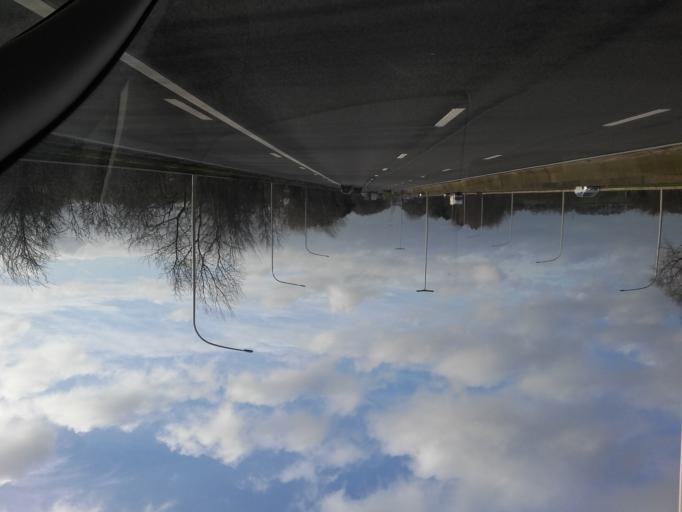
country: BE
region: Wallonia
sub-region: Province du Brabant Wallon
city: Louvain-la-Neuve
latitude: 50.6607
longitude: 4.6534
